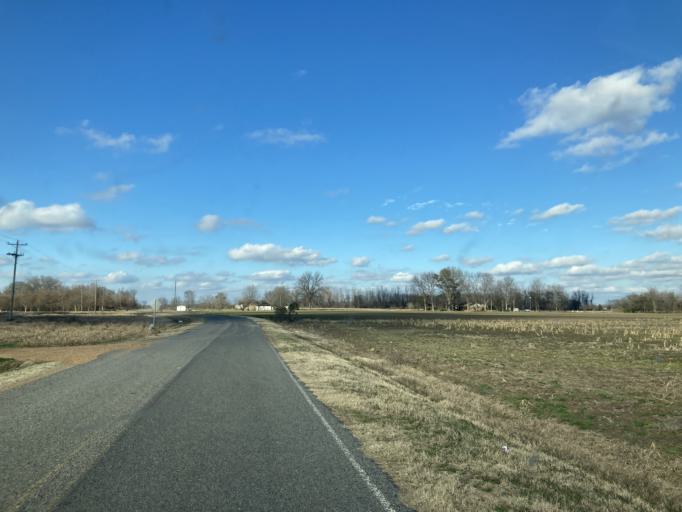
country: US
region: Mississippi
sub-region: Yazoo County
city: Yazoo City
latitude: 32.9285
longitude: -90.4716
